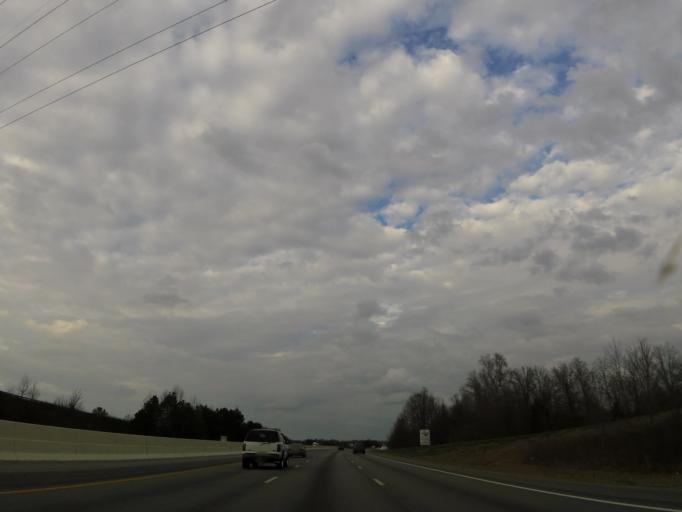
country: US
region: South Carolina
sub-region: Greenville County
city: Mauldin
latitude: 34.7570
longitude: -82.2849
